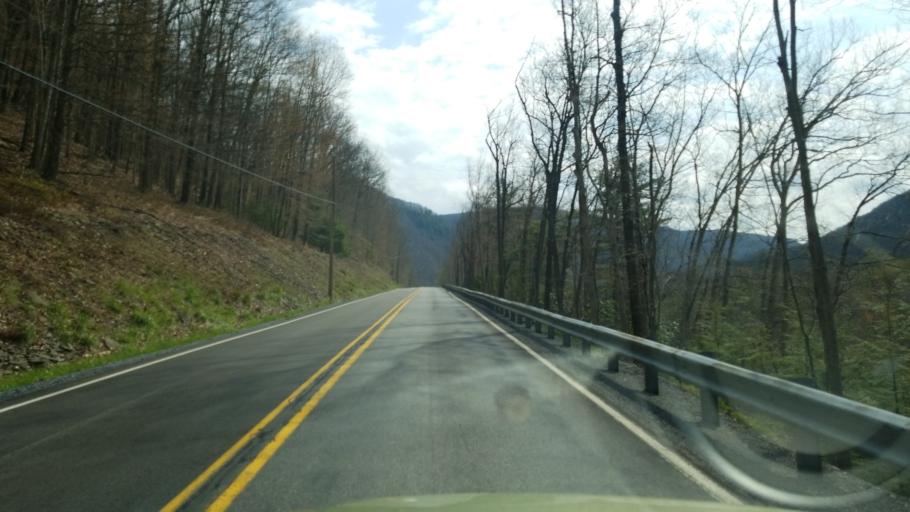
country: US
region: Pennsylvania
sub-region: Clinton County
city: Renovo
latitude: 41.3000
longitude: -77.9982
